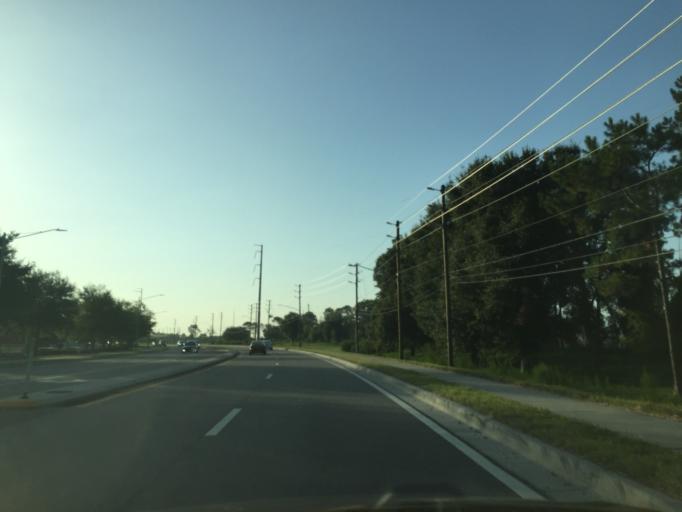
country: US
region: Florida
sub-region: Orange County
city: Alafaya
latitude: 28.5255
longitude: -81.2029
